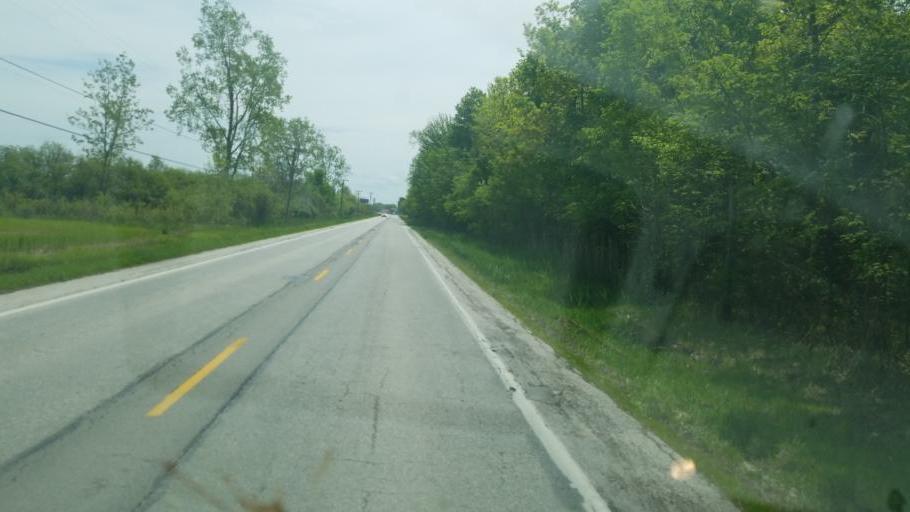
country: US
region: Ohio
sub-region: Ottawa County
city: Oak Harbor
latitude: 41.5486
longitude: -83.0553
